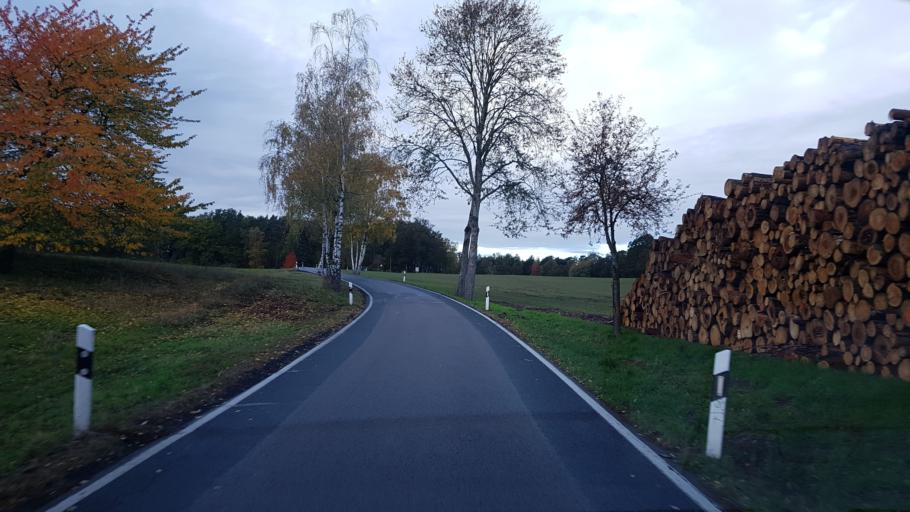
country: DE
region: Saxony
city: Dahlen
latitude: 51.3900
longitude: 13.0250
